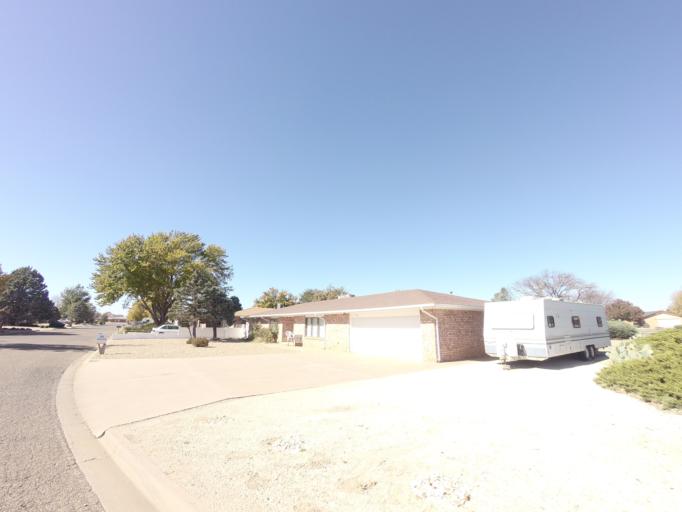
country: US
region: New Mexico
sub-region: Curry County
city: Clovis
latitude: 34.4226
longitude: -103.1899
